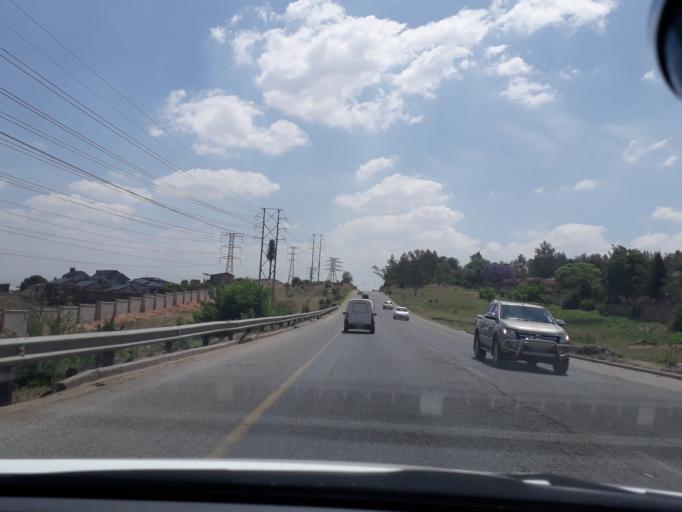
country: ZA
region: Gauteng
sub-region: City of Johannesburg Metropolitan Municipality
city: Midrand
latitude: -26.0067
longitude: 28.0965
